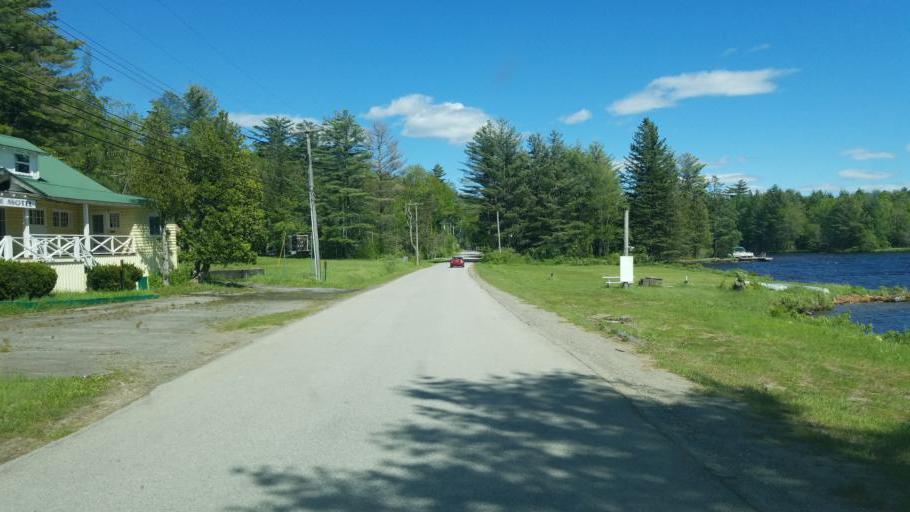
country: US
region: New York
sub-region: Fulton County
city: Gloversville
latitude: 43.1639
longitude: -74.4991
